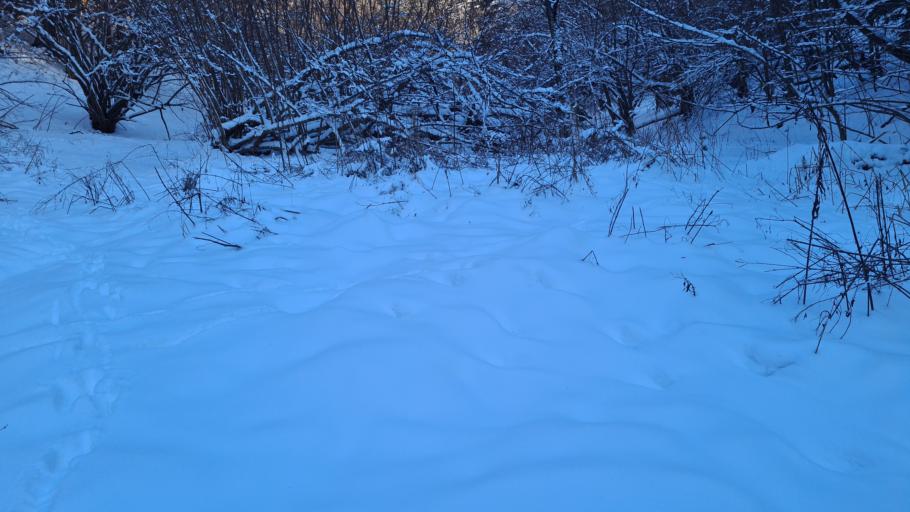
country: HR
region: Varazdinska
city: Ivanec
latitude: 46.1792
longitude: 16.1006
